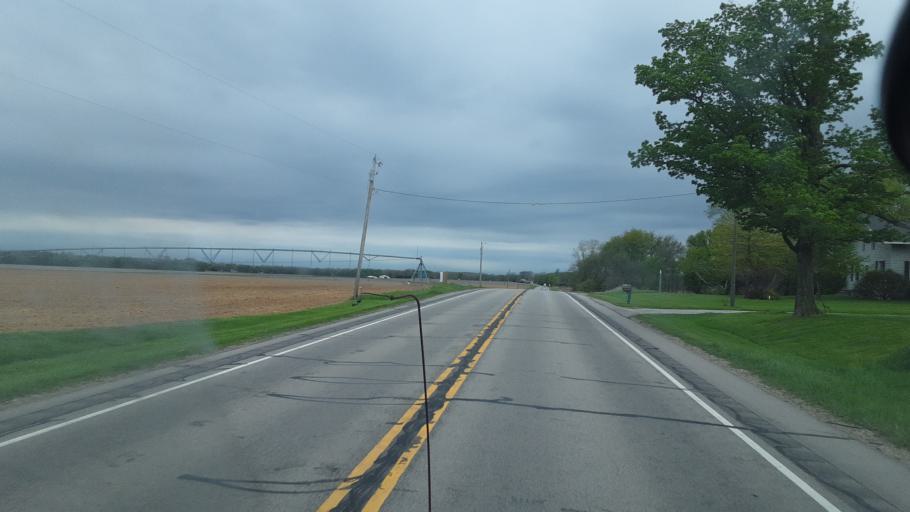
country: US
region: Indiana
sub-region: Kosciusko County
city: Syracuse
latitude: 41.4929
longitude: -85.7223
